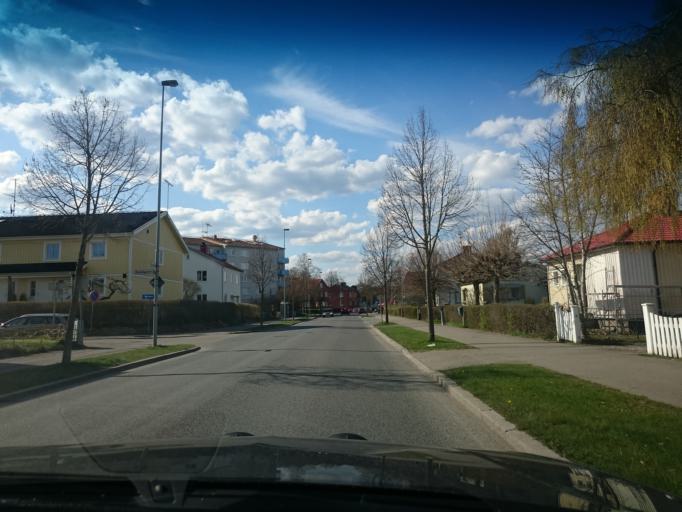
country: SE
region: Joenkoeping
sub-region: Vetlanda Kommun
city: Vetlanda
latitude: 57.4265
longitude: 15.0713
